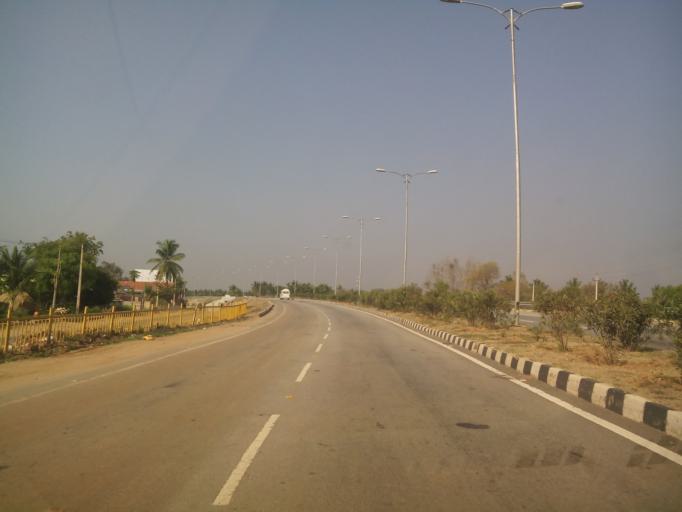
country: IN
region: Karnataka
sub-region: Tumkur
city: Kunigal
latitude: 13.0303
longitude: 77.0795
